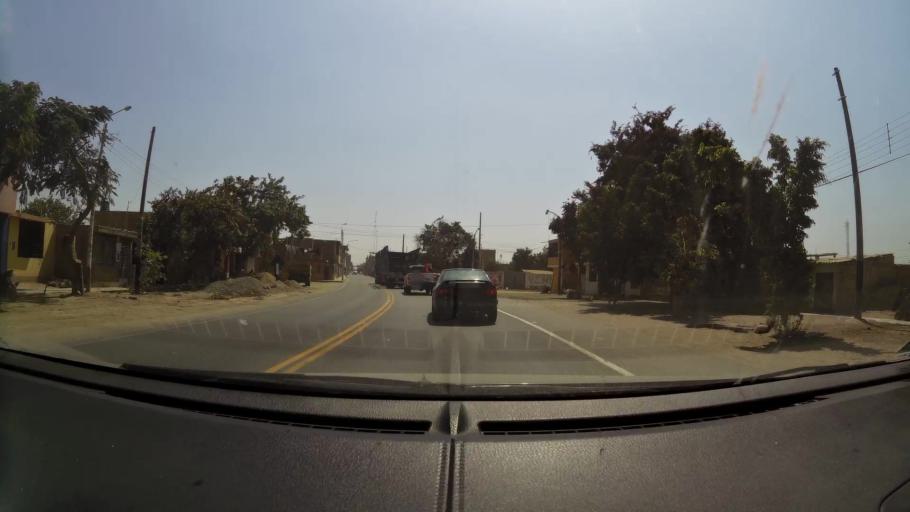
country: PE
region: Lambayeque
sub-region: Provincia de Chiclayo
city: Mocupe
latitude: -6.9913
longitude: -79.6206
